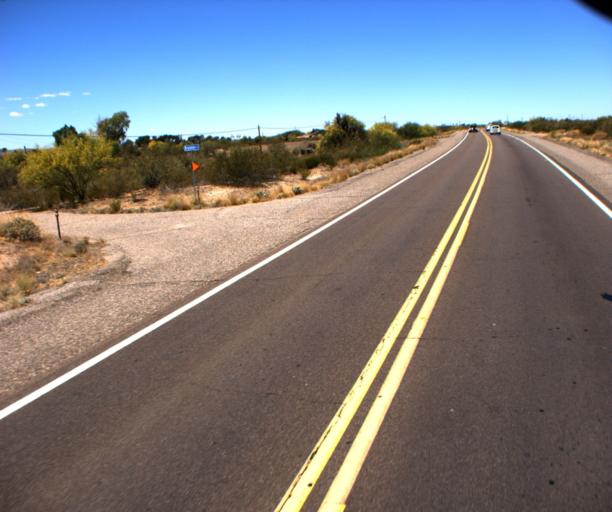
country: US
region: Arizona
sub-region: Maricopa County
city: Wickenburg
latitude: 33.9994
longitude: -112.7619
